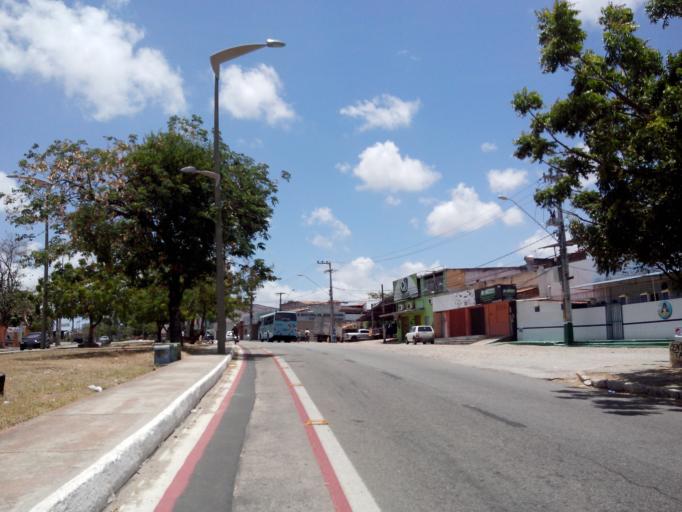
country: BR
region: Ceara
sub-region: Caucaia
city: Caucaia
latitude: -3.7694
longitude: -38.6071
